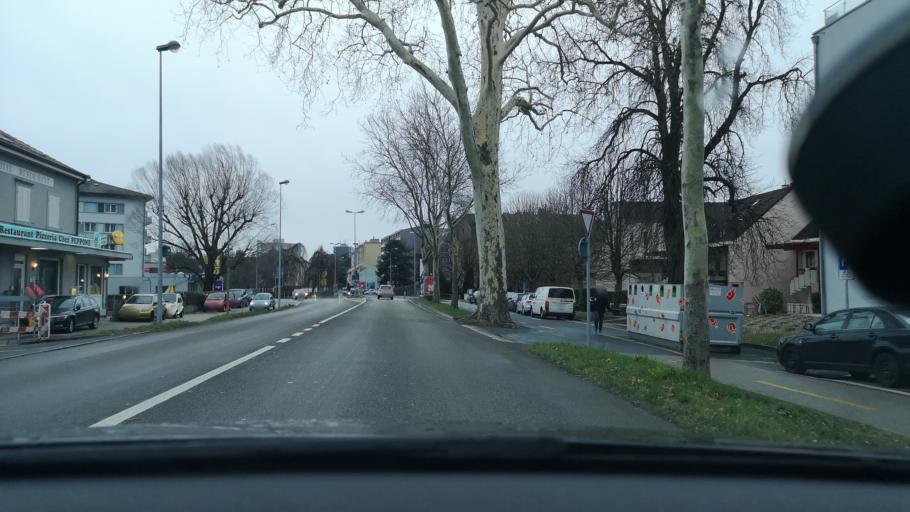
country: CH
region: Vaud
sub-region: Jura-Nord vaudois District
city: Yverdon-les-Bains
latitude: 46.7858
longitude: 6.6323
